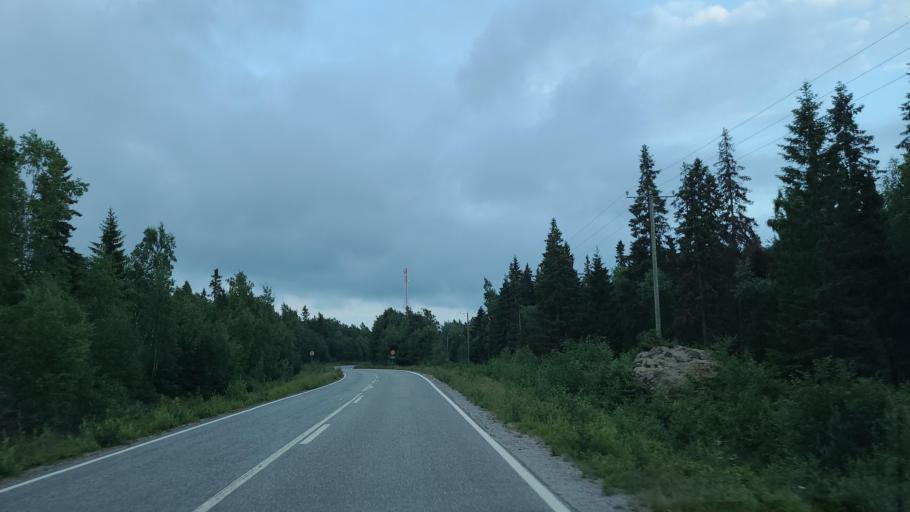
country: FI
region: Ostrobothnia
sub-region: Vaasa
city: Replot
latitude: 63.2902
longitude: 21.1118
